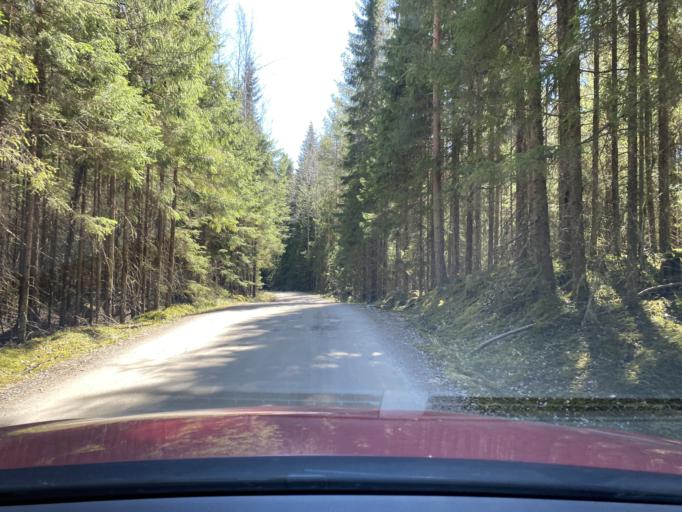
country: FI
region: Uusimaa
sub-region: Helsinki
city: Kaerkoelae
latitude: 60.6600
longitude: 23.8686
